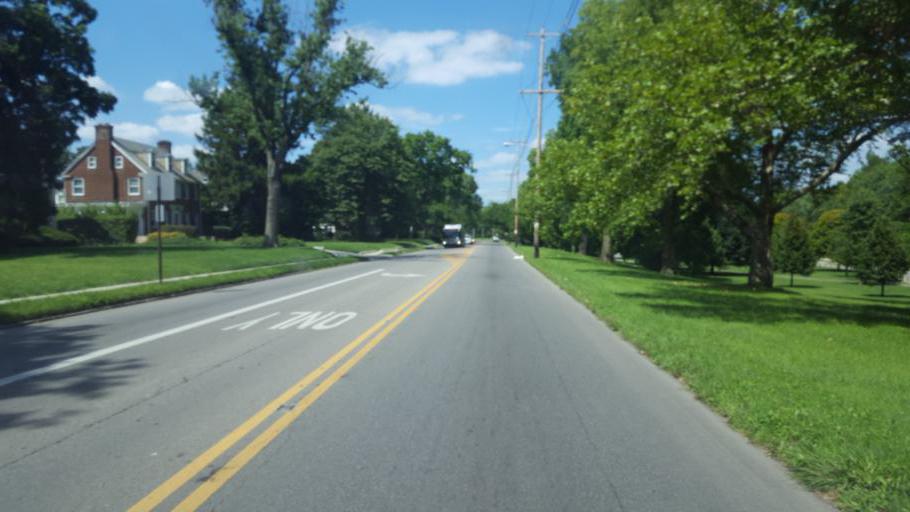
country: US
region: Ohio
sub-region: Franklin County
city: Bexley
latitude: 39.9717
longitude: -82.9489
